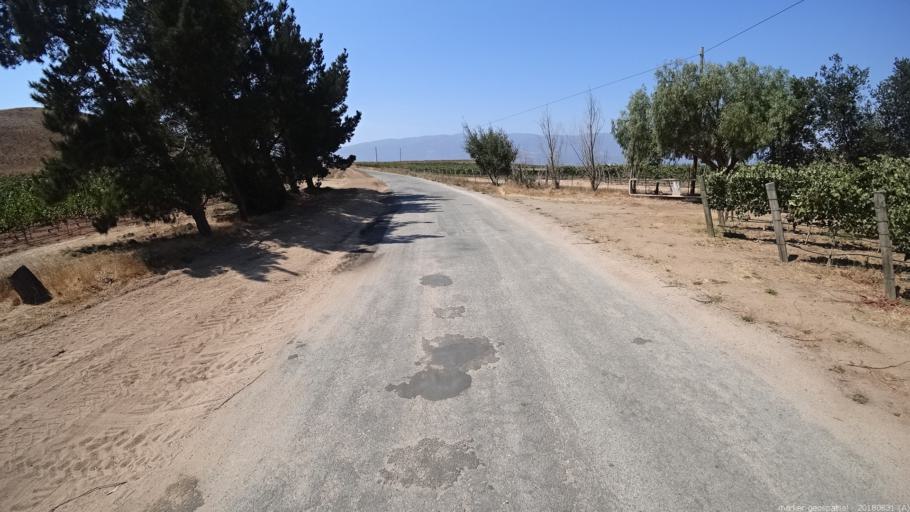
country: US
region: California
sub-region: Monterey County
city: Soledad
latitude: 36.4466
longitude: -121.3017
